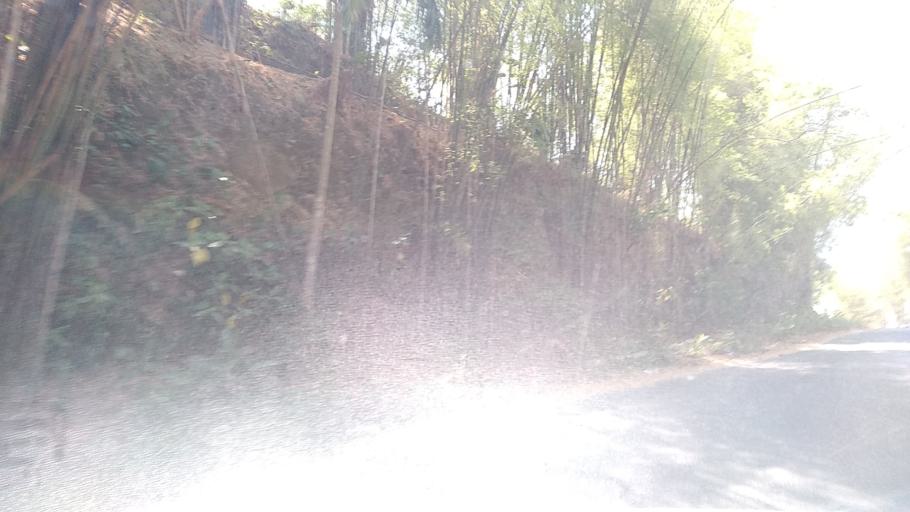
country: ID
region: Central Java
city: Ungaran
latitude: -7.1087
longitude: 110.4021
